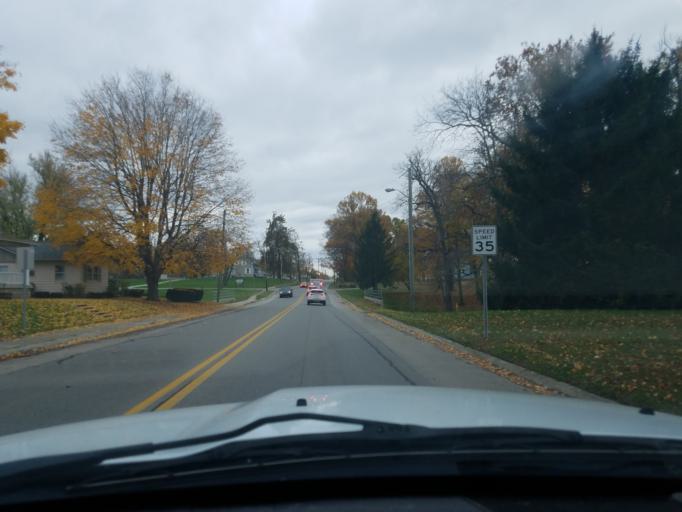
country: US
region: Indiana
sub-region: Bartholomew County
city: Hope
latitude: 39.2996
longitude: -85.7715
